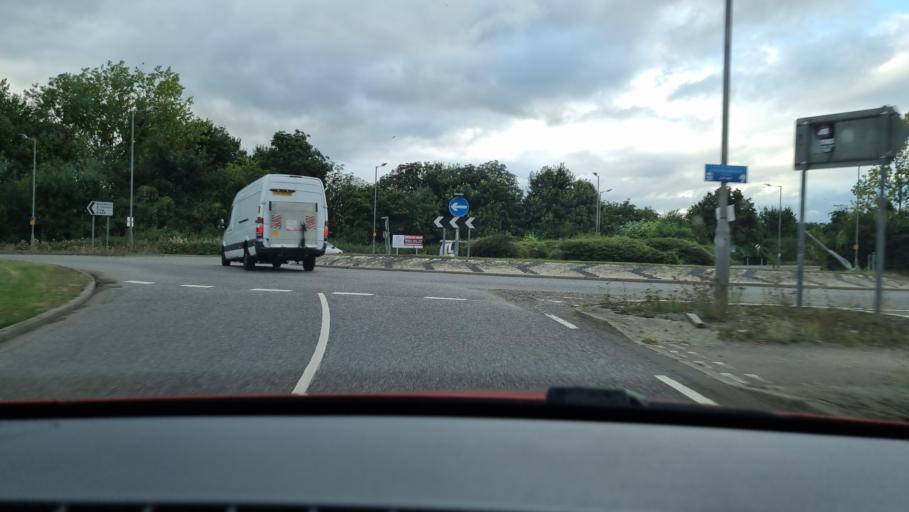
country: GB
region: England
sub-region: Buckinghamshire
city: Ivinghoe
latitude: 51.8181
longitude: -0.6359
